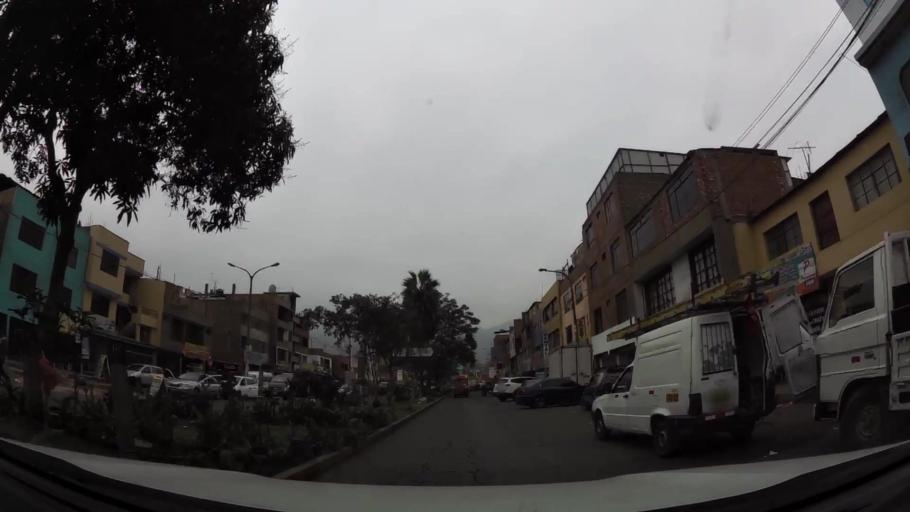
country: PE
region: Lima
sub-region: Lima
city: Independencia
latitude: -11.9835
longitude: -77.0602
